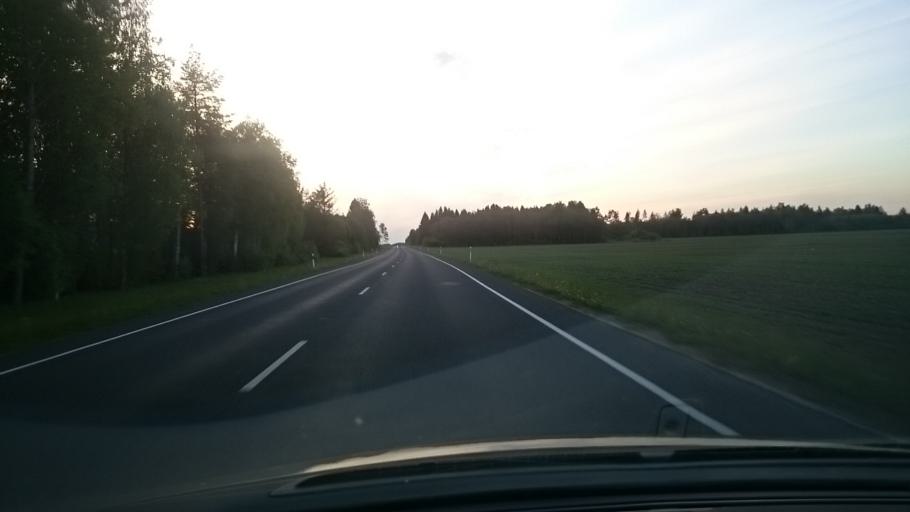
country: EE
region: Viljandimaa
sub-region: Vohma linn
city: Vohma
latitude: 58.7124
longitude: 25.6152
